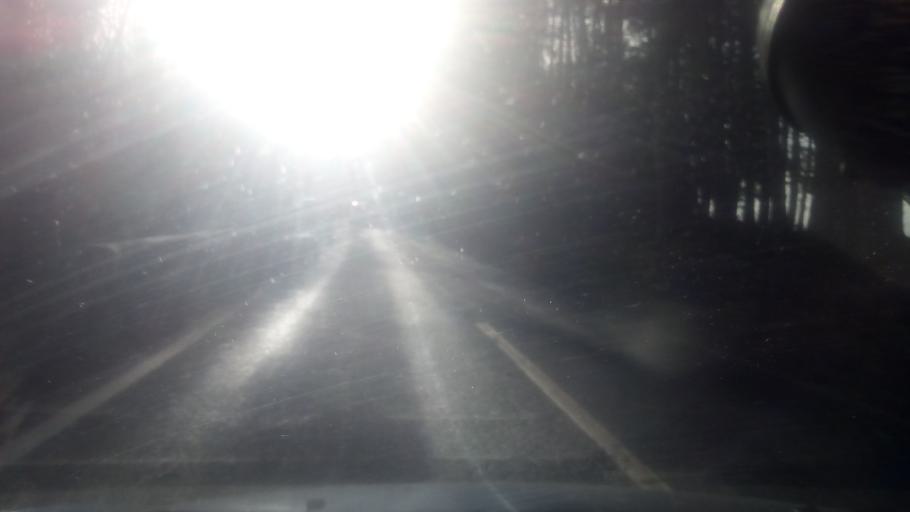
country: GB
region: Scotland
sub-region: The Scottish Borders
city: Jedburgh
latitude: 55.4086
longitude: -2.5073
